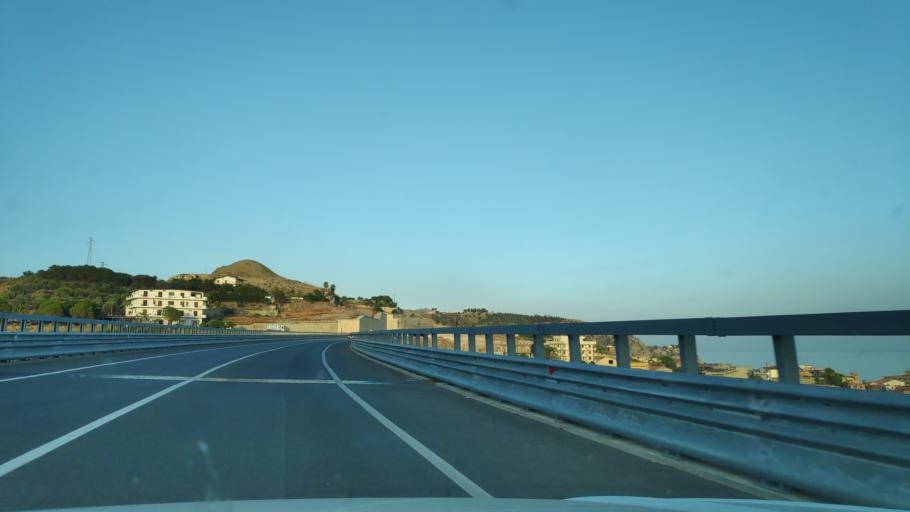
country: IT
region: Calabria
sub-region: Provincia di Reggio Calabria
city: Bova Marina
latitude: 37.9349
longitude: 15.9163
